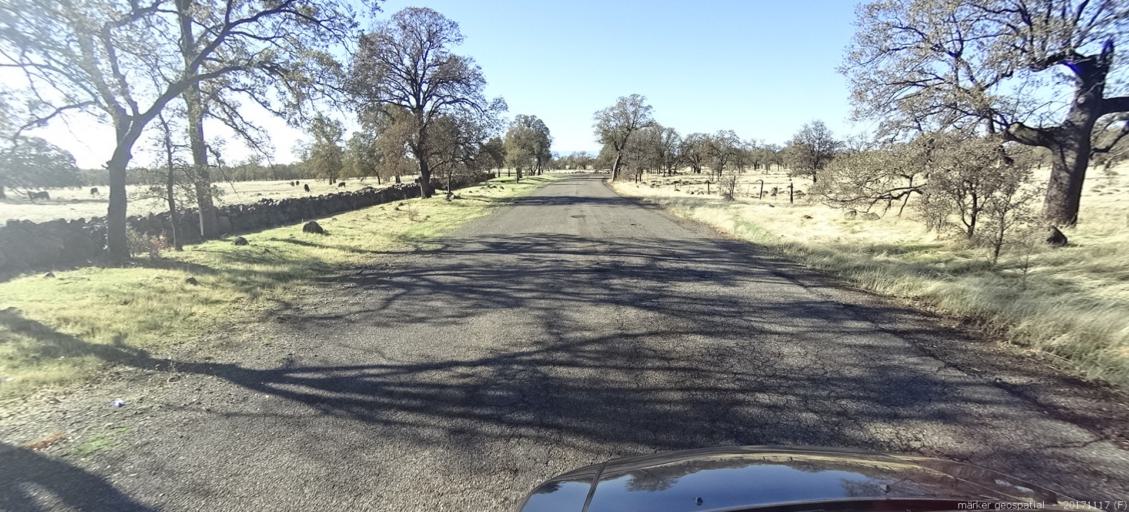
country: US
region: California
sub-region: Shasta County
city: Palo Cedro
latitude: 40.4610
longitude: -122.1021
